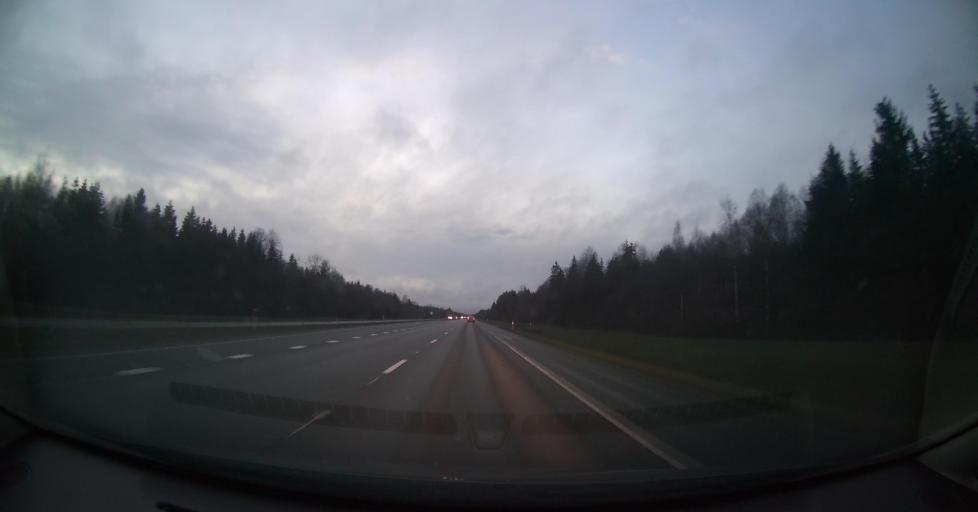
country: EE
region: Laeaene-Virumaa
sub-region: Tapa vald
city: Tapa
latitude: 59.4553
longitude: 25.9163
